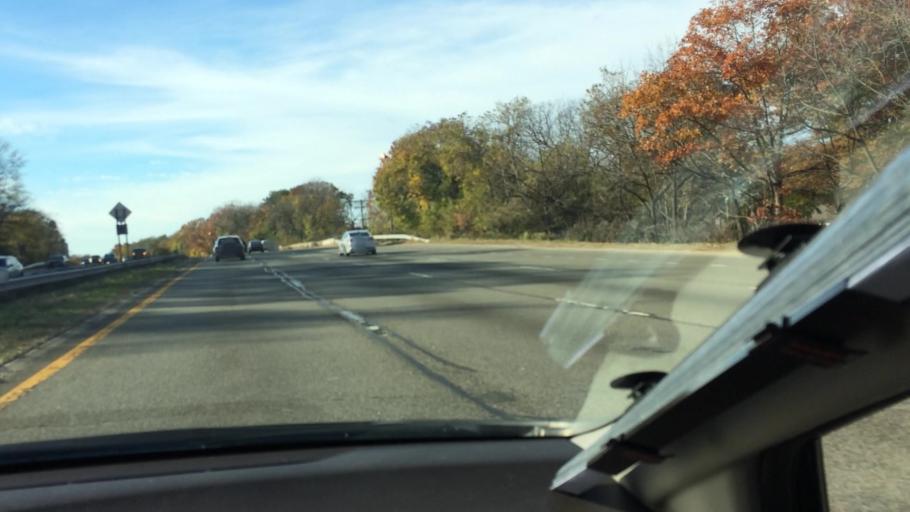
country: US
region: New York
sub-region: Nassau County
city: Malverne
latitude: 40.6827
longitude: -73.6659
